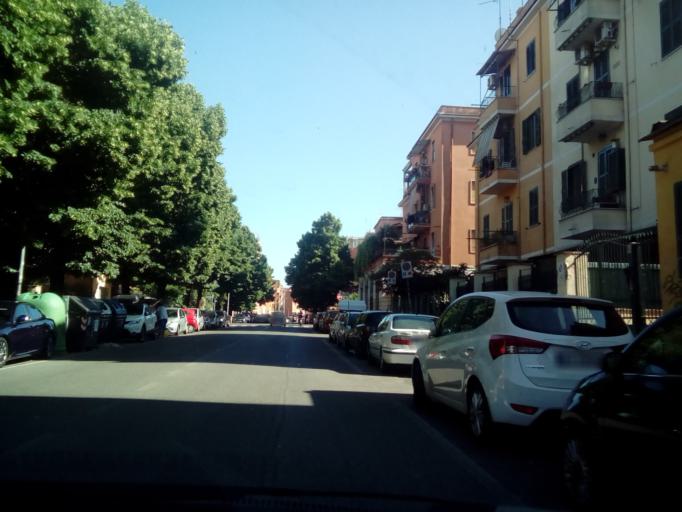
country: IT
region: Latium
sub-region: Citta metropolitana di Roma Capitale
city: Rome
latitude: 41.8896
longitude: 12.5669
